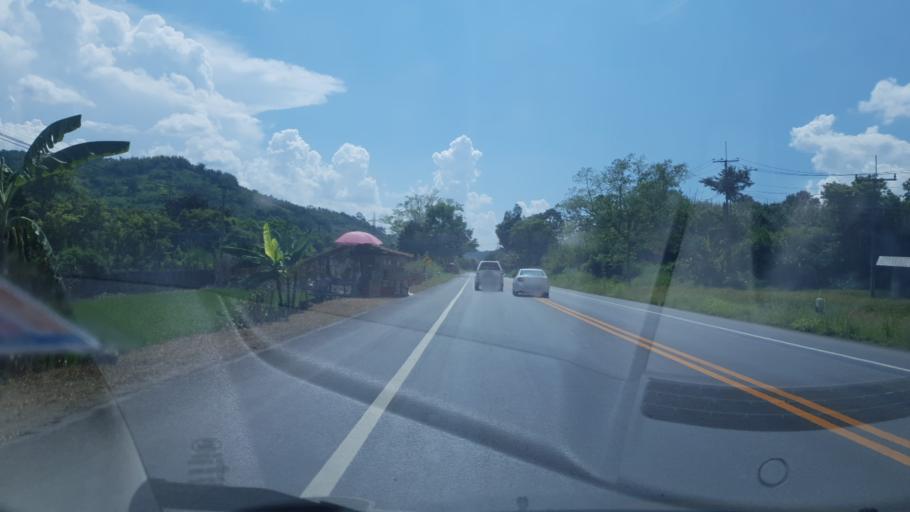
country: TH
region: Chiang Rai
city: Mae Suai
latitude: 19.7172
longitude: 99.5998
